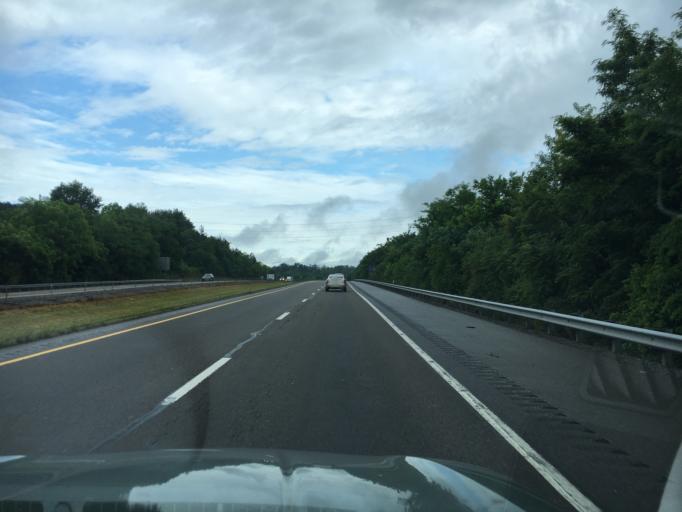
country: US
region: Tennessee
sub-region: Cocke County
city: Newport
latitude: 35.9649
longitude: -83.2200
